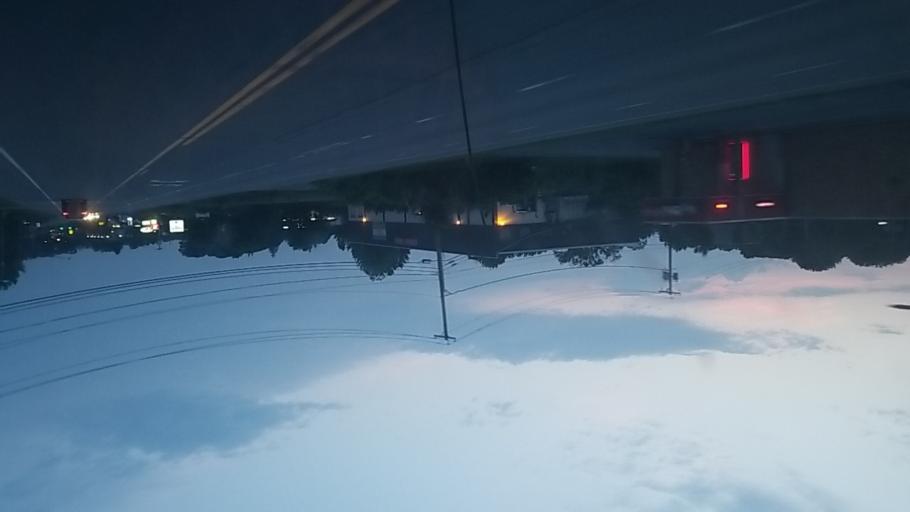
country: US
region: New York
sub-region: Fulton County
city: Johnstown
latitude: 43.0163
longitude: -74.3612
